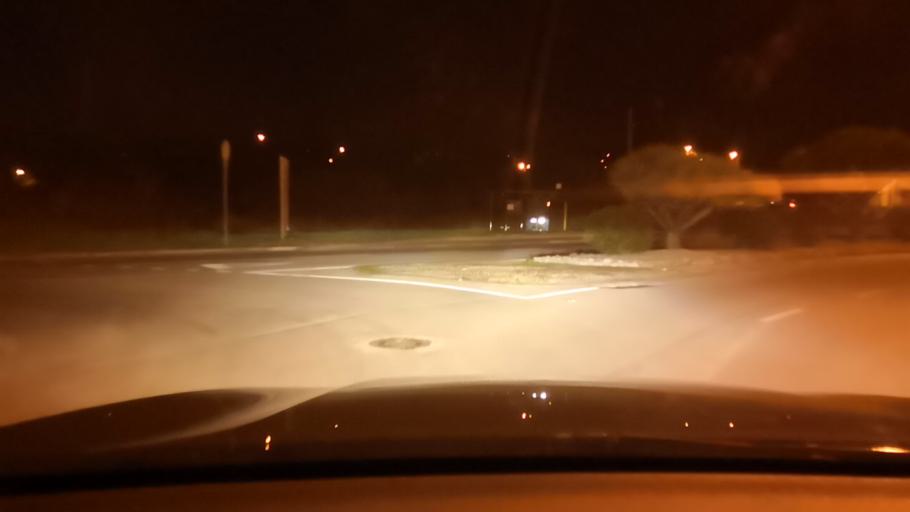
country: PT
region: Setubal
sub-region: Setubal
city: Setubal
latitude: 38.5447
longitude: -8.8562
